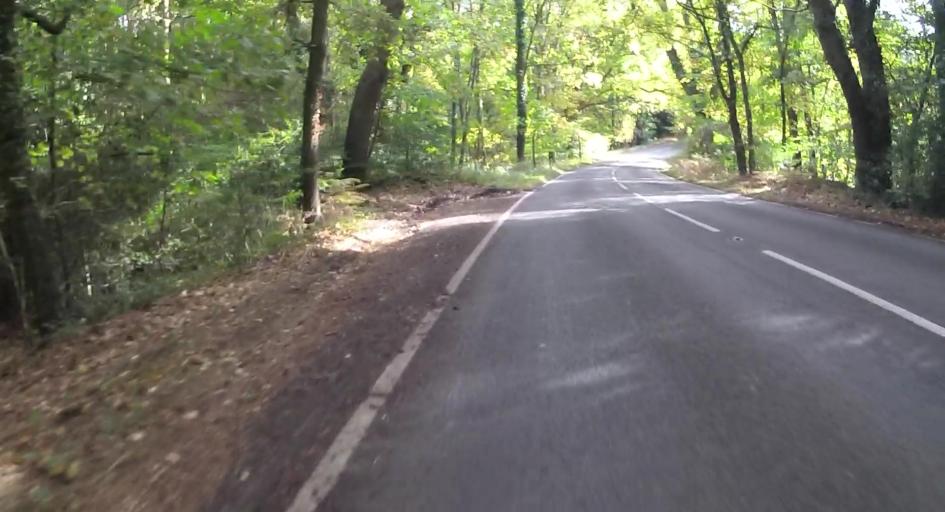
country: GB
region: England
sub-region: Surrey
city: Seale
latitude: 51.2028
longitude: -0.7442
